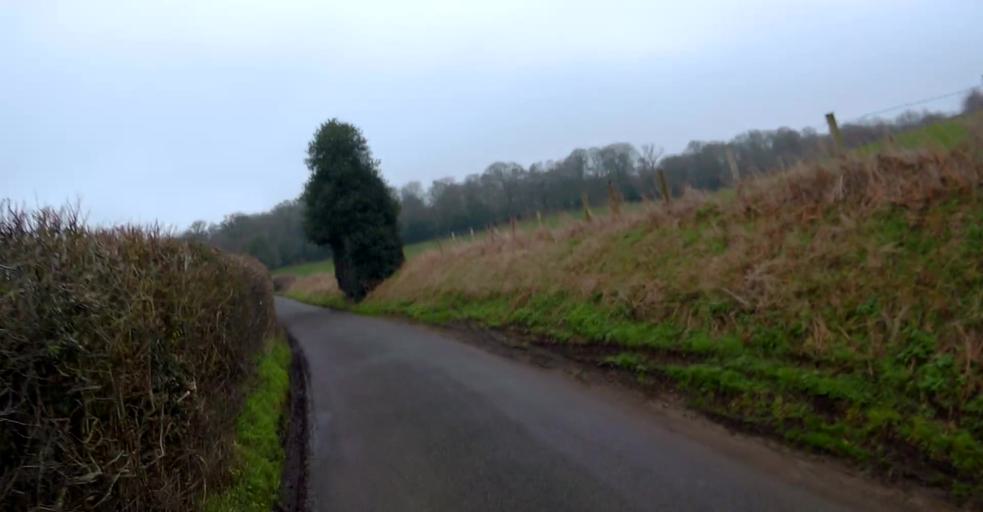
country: GB
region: England
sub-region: Hampshire
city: Hook
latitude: 51.3207
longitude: -0.9347
